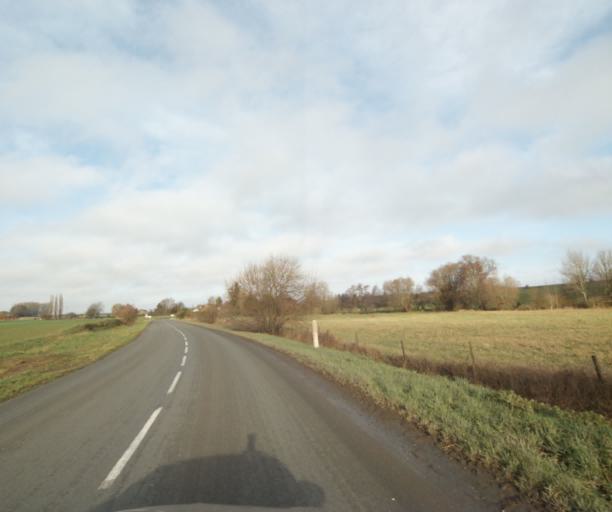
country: FR
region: Nord-Pas-de-Calais
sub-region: Departement du Nord
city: Thiant
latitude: 50.2783
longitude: 3.4536
